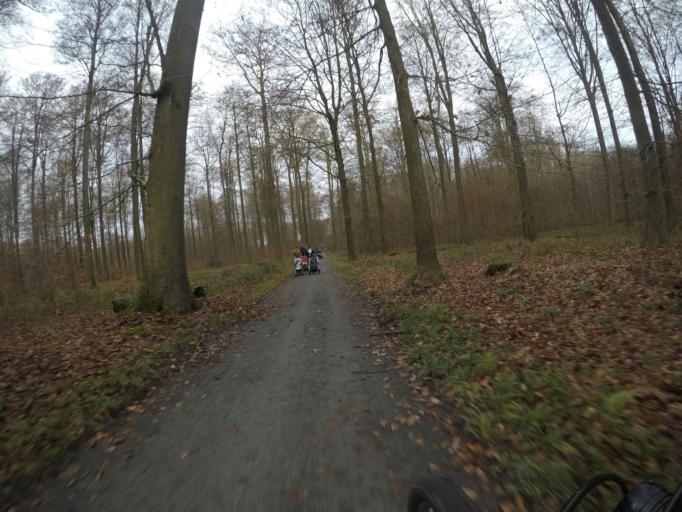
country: BE
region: Flanders
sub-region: Provincie Vlaams-Brabant
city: Hoeilaart
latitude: 50.7503
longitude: 4.4359
